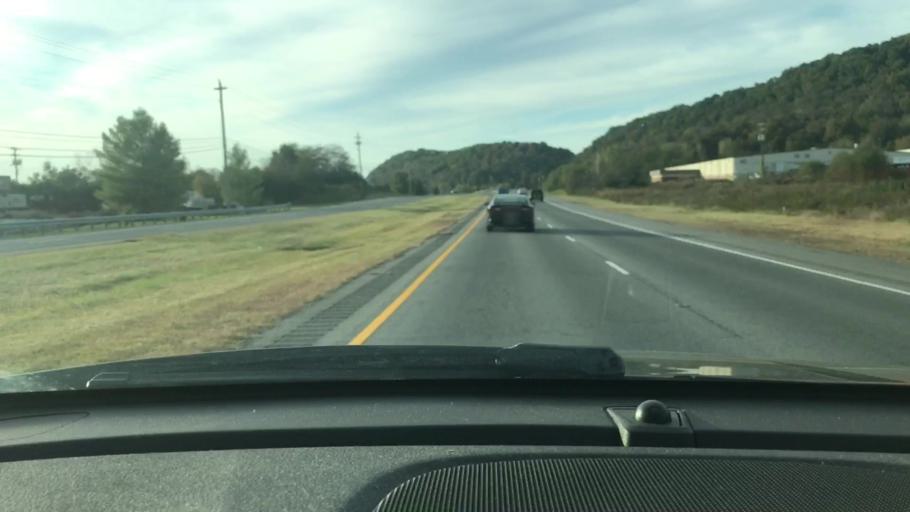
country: US
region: Tennessee
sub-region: Cheatham County
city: Ashland City
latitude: 36.2261
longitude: -87.0094
